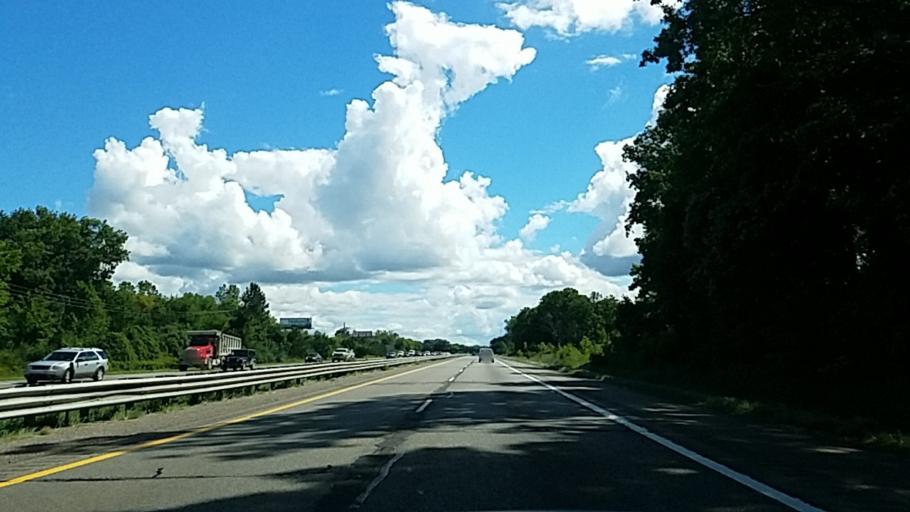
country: US
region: Michigan
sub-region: Livingston County
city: Whitmore Lake
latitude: 42.3863
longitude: -83.7613
